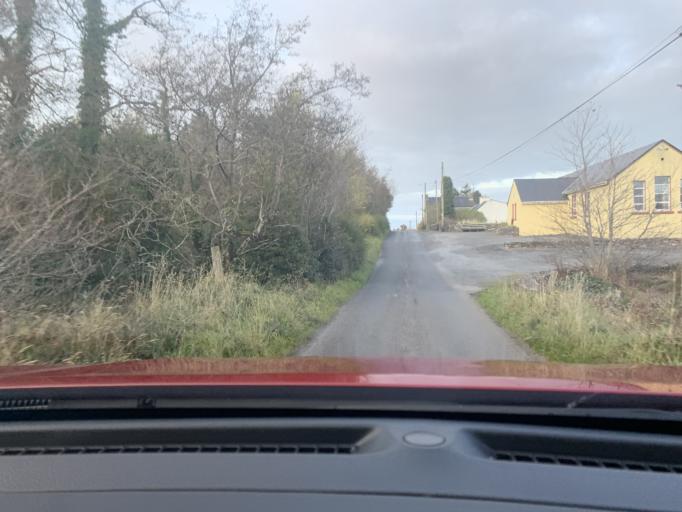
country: IE
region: Connaught
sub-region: Roscommon
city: Ballaghaderreen
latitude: 53.9746
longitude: -8.6213
